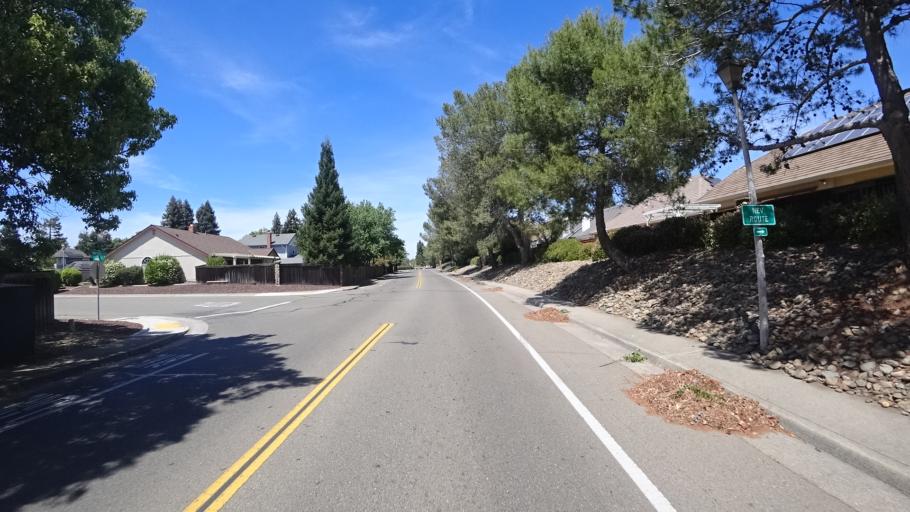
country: US
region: California
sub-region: Placer County
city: Rocklin
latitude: 38.8055
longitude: -121.2541
